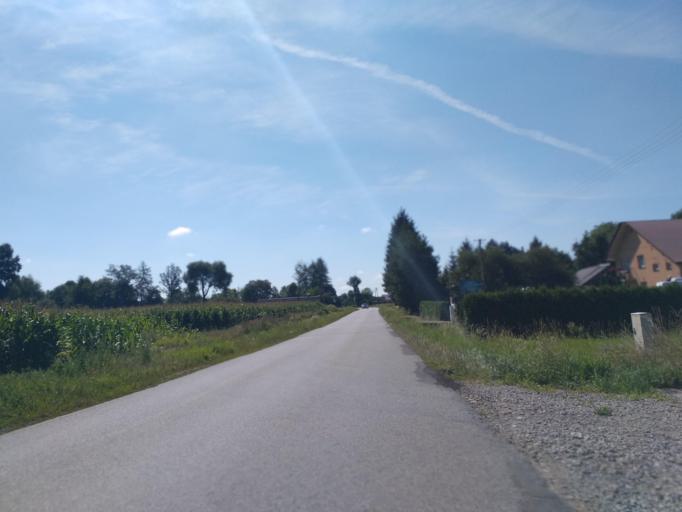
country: PL
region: Subcarpathian Voivodeship
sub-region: Powiat brzozowski
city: Gorki
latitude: 49.6257
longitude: 22.0112
